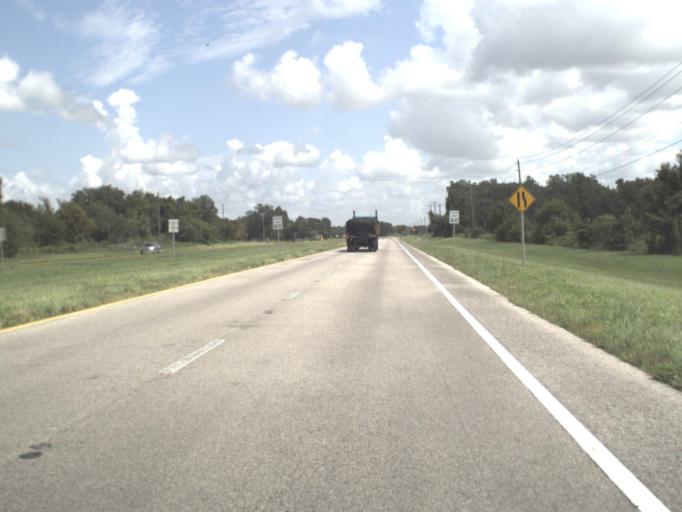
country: US
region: Florida
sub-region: DeSoto County
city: Arcadia
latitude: 27.3331
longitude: -81.8086
